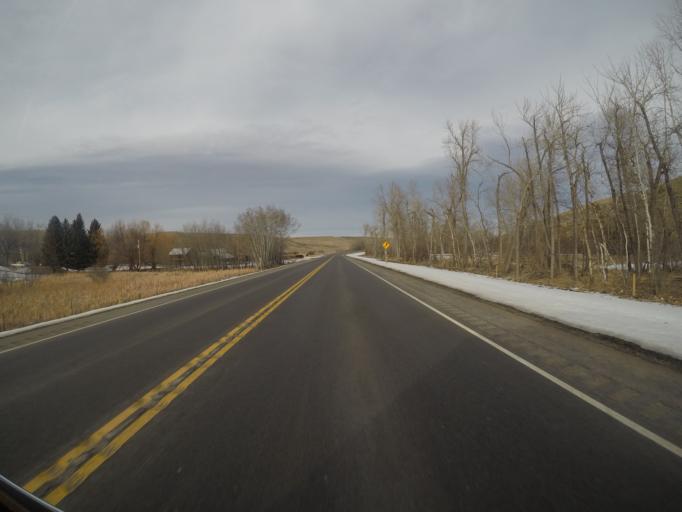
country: US
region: Montana
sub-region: Stillwater County
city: Absarokee
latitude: 45.4304
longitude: -109.4700
